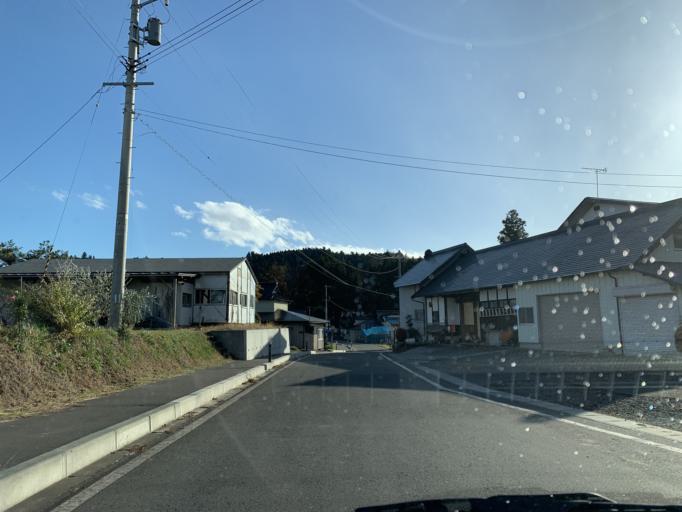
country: JP
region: Iwate
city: Ichinoseki
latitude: 39.0091
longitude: 141.0968
